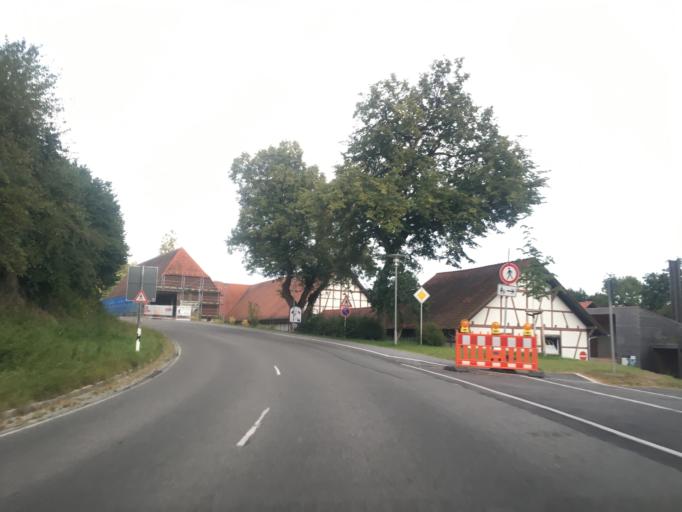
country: DE
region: Baden-Wuerttemberg
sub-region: Tuebingen Region
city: Gomadingen
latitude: 48.3844
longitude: 9.4161
